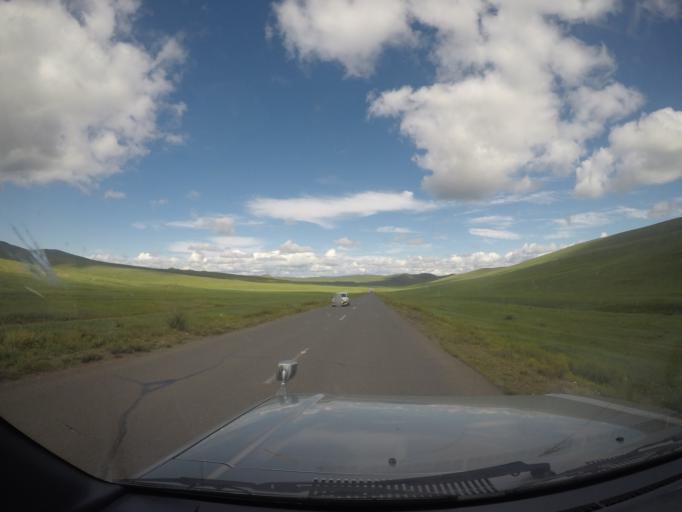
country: MN
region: Hentiy
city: Bayanbulag
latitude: 47.4529
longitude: 109.7947
